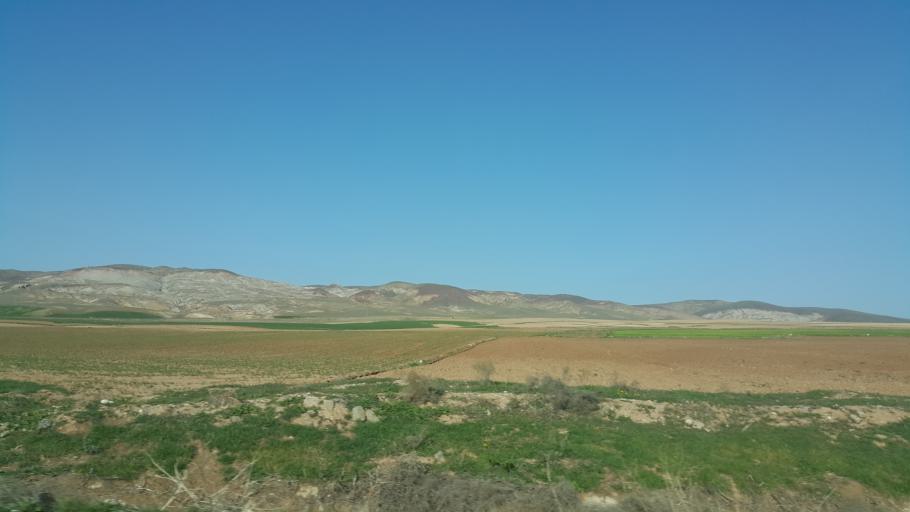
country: TR
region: Ankara
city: Sereflikochisar
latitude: 38.7192
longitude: 33.6748
